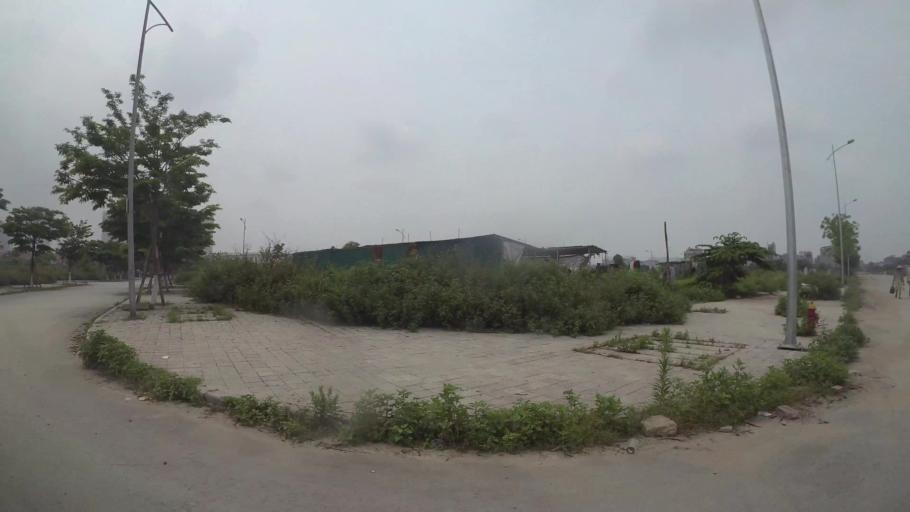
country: VN
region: Ha Noi
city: Ha Dong
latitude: 20.9786
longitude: 105.7516
